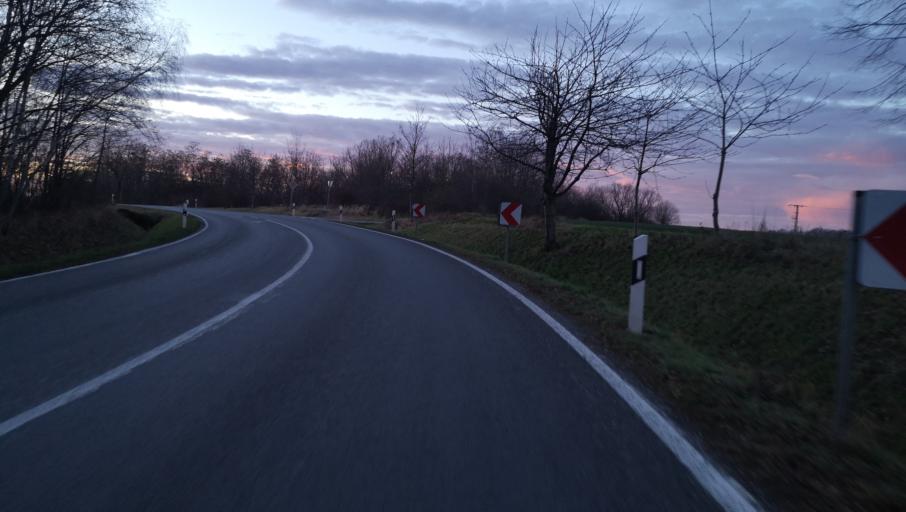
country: DE
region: Thuringia
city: Ronneburg
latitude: 50.8638
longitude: 12.1660
